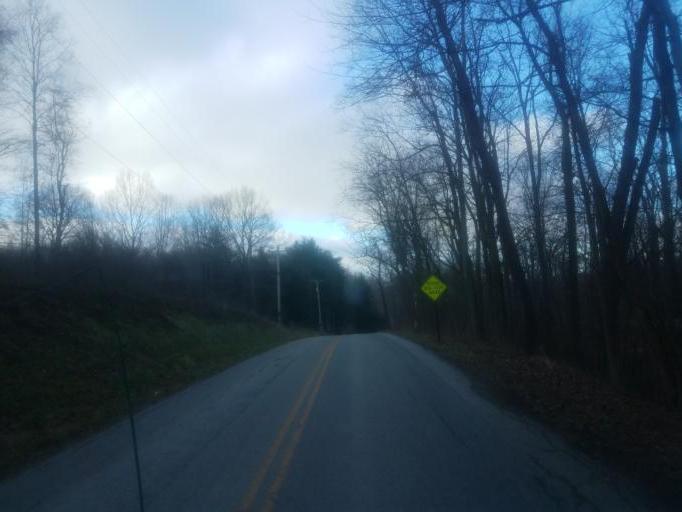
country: US
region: Ohio
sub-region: Sandusky County
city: Bellville
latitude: 40.5962
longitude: -82.3745
